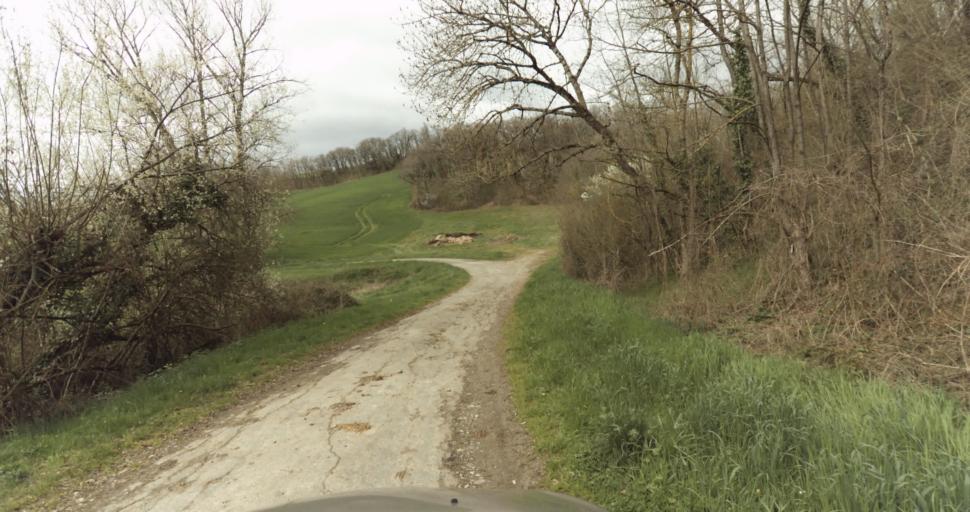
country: FR
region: Midi-Pyrenees
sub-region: Departement du Tarn
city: Puygouzon
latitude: 43.8789
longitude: 2.1647
